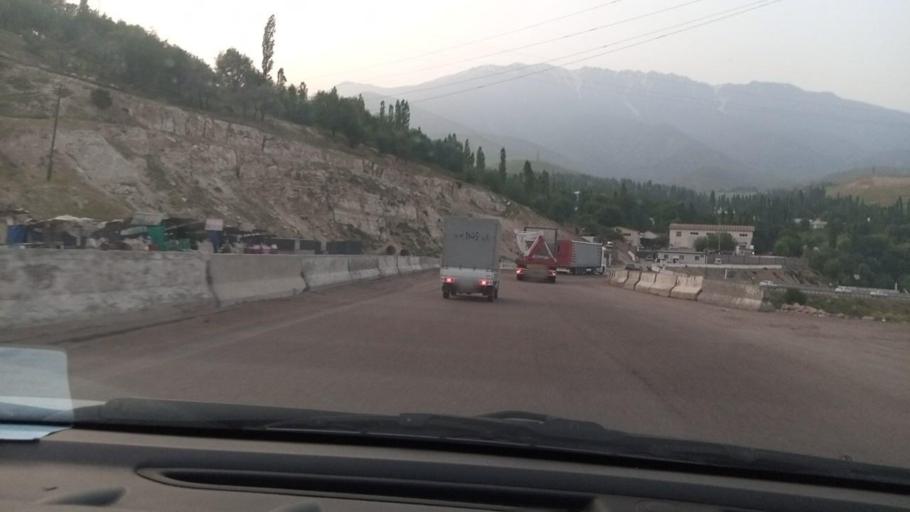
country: UZ
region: Toshkent
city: Angren
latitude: 41.0731
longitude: 70.2518
